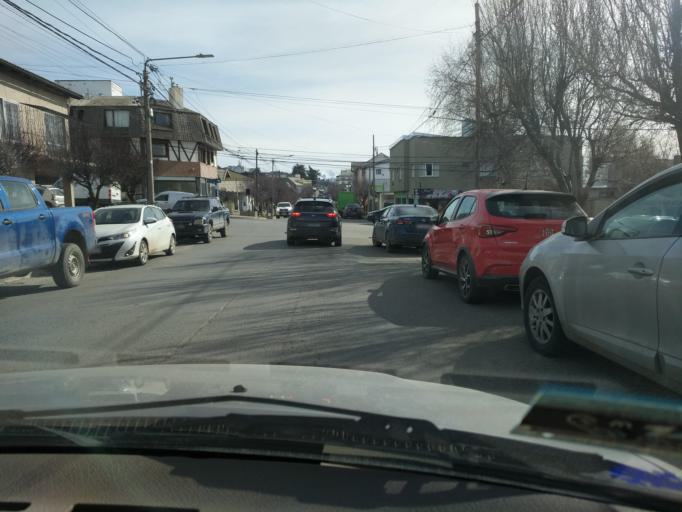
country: AR
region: Rio Negro
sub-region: Departamento de Bariloche
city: San Carlos de Bariloche
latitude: -41.1373
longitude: -71.2941
